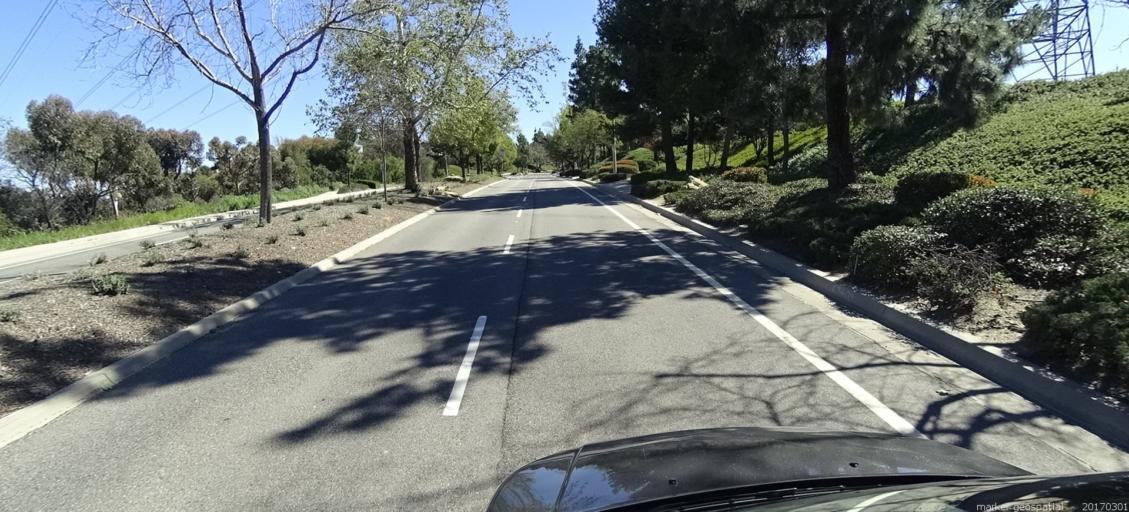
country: US
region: California
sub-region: Orange County
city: Villa Park
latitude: 33.8478
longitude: -117.7593
